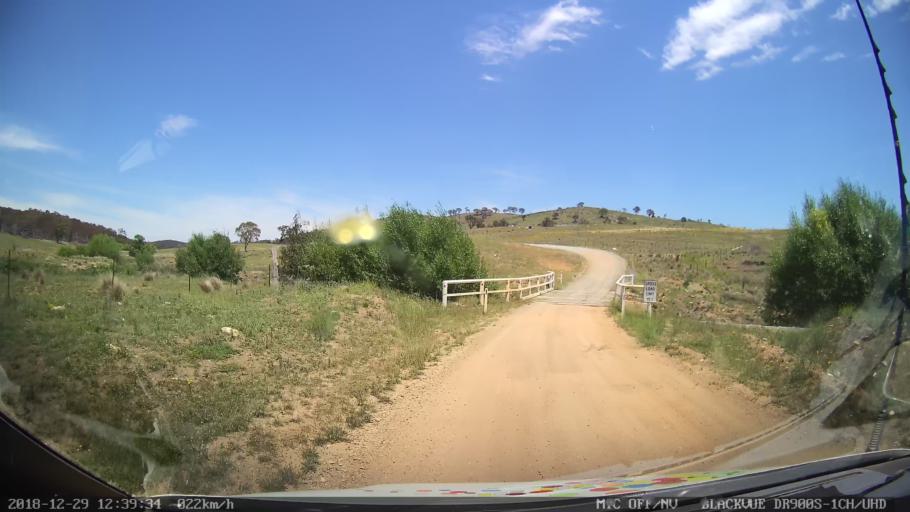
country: AU
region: Australian Capital Territory
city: Macarthur
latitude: -35.5974
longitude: 149.2270
